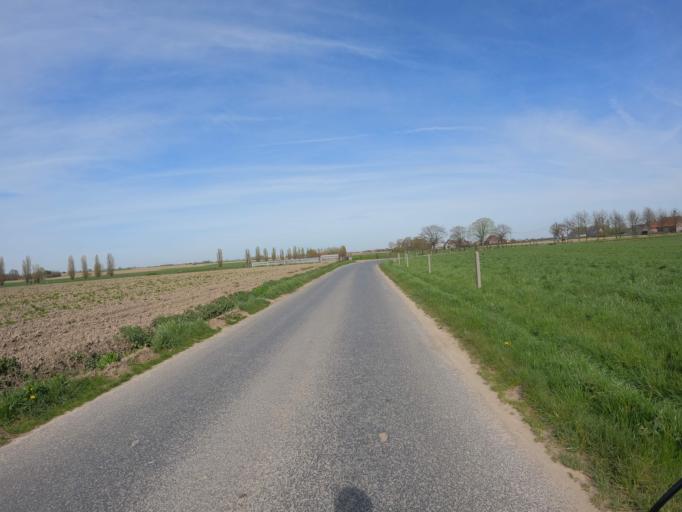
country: BE
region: Flanders
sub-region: Provincie West-Vlaanderen
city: Tielt
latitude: 51.0115
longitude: 3.3421
